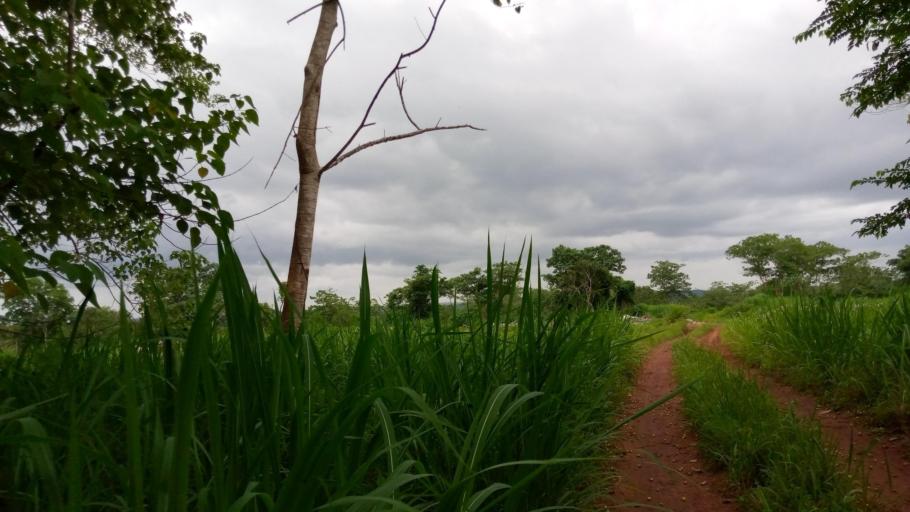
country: SL
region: Southern Province
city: Moyamba
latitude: 8.1655
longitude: -12.4671
